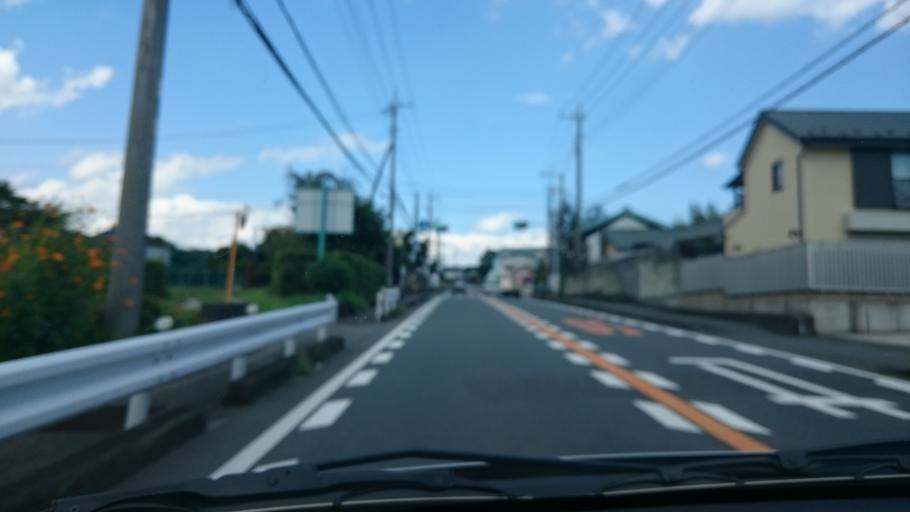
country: JP
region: Shizuoka
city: Gotemba
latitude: 35.2315
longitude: 138.9208
